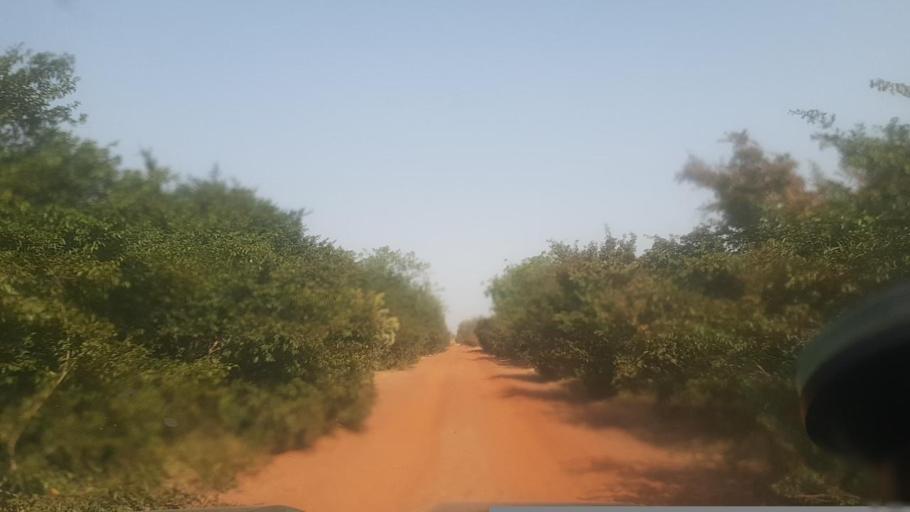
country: ML
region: Segou
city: Bla
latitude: 12.8526
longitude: -5.9821
